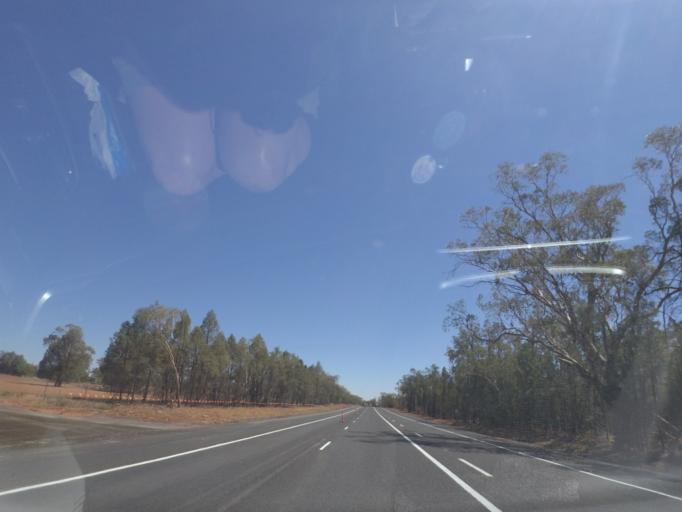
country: AU
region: New South Wales
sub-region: Gilgandra
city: Gilgandra
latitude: -31.6602
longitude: 148.7232
